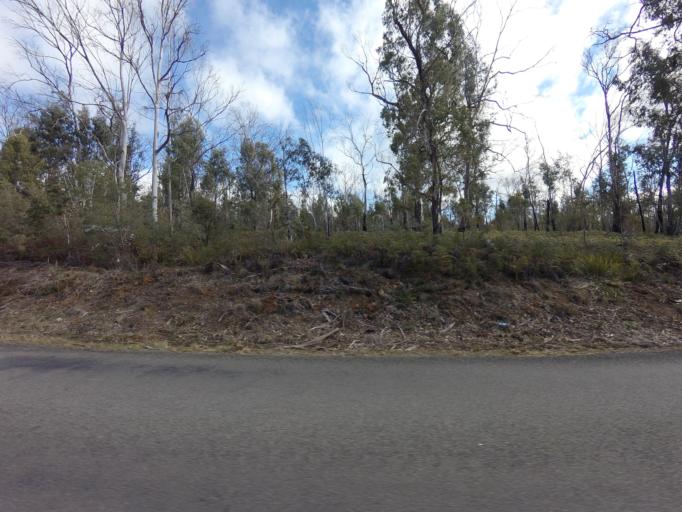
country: AU
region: Tasmania
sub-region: Derwent Valley
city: New Norfolk
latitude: -42.5492
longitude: 146.7144
